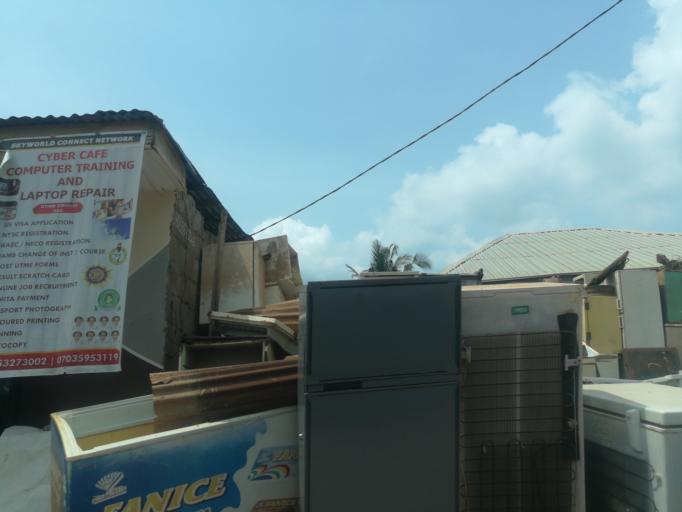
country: NG
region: Oyo
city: Moniya
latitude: 7.4539
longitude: 3.9576
